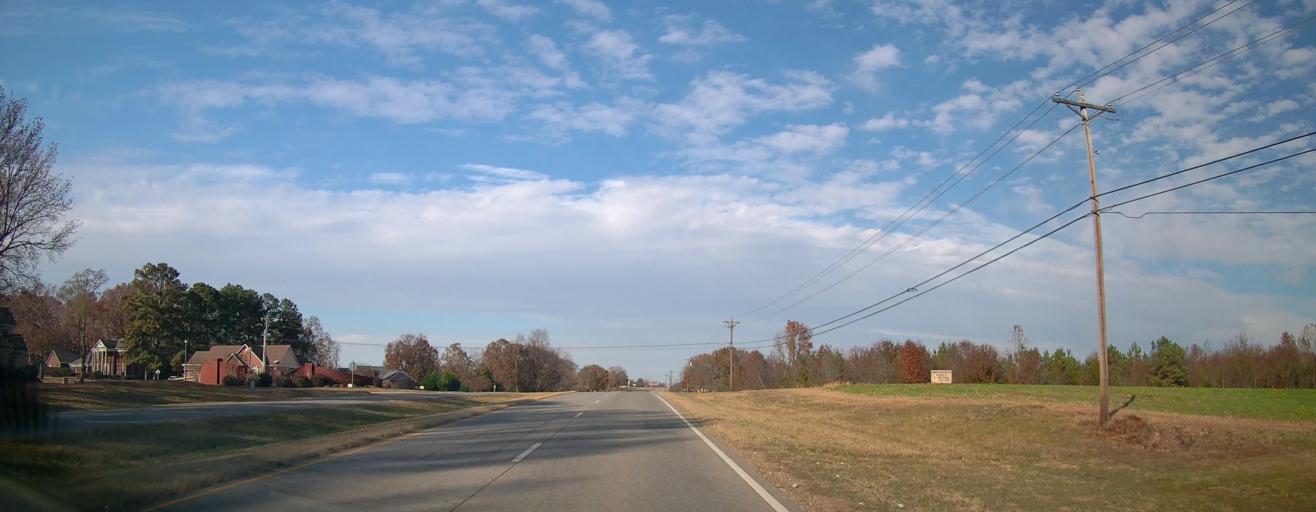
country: US
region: Alabama
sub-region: Limestone County
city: Athens
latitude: 34.7208
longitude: -86.9567
